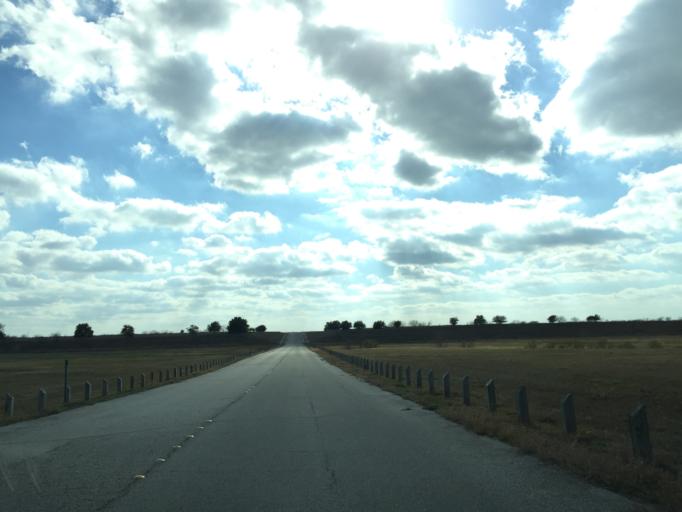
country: US
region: Texas
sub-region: Williamson County
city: Granger
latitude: 30.6834
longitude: -97.3392
